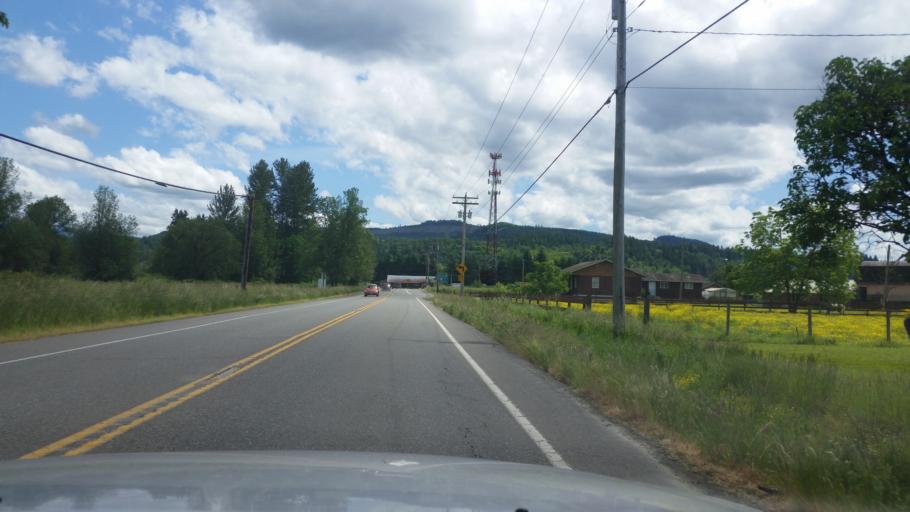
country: US
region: Washington
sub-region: Pierce County
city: Orting
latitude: 47.0834
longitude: -122.1901
